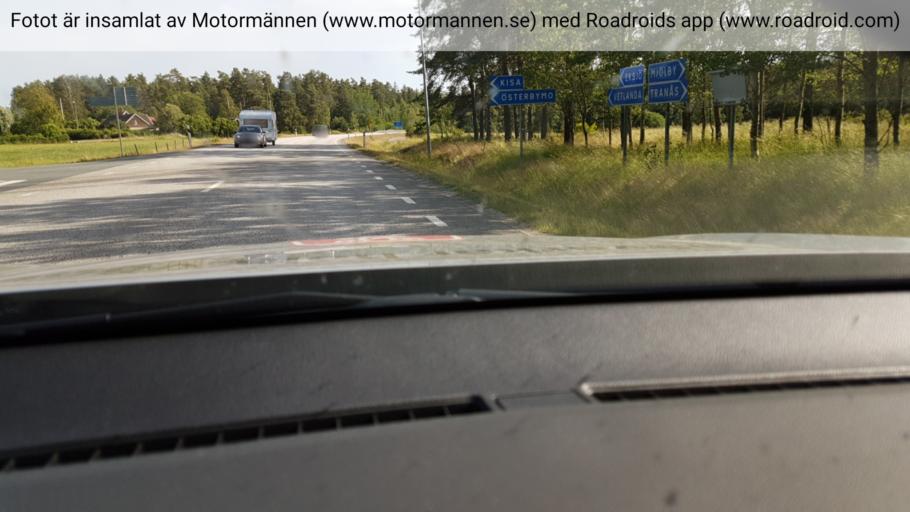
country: SE
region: Joenkoeping
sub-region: Eksjo Kommun
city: Eksjoe
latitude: 57.6913
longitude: 14.9549
